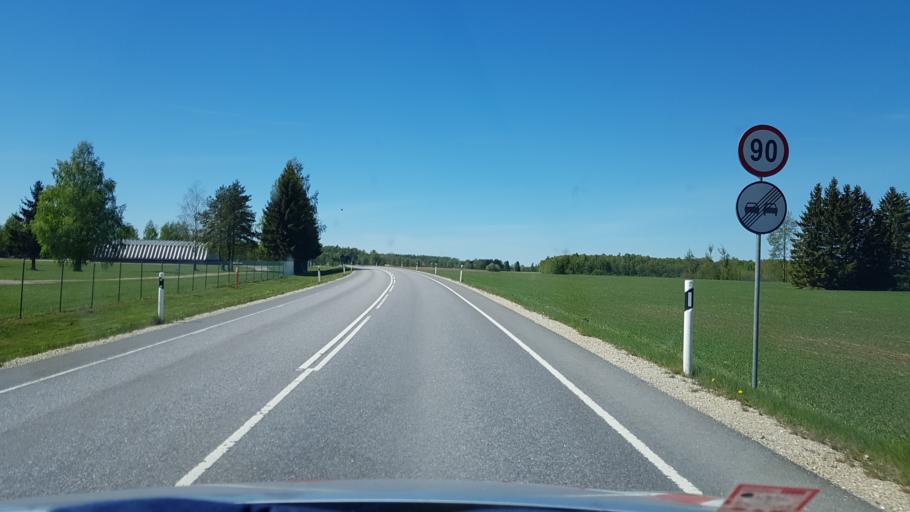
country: EE
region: Tartu
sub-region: UElenurme vald
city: Ulenurme
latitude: 58.3118
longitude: 26.6895
